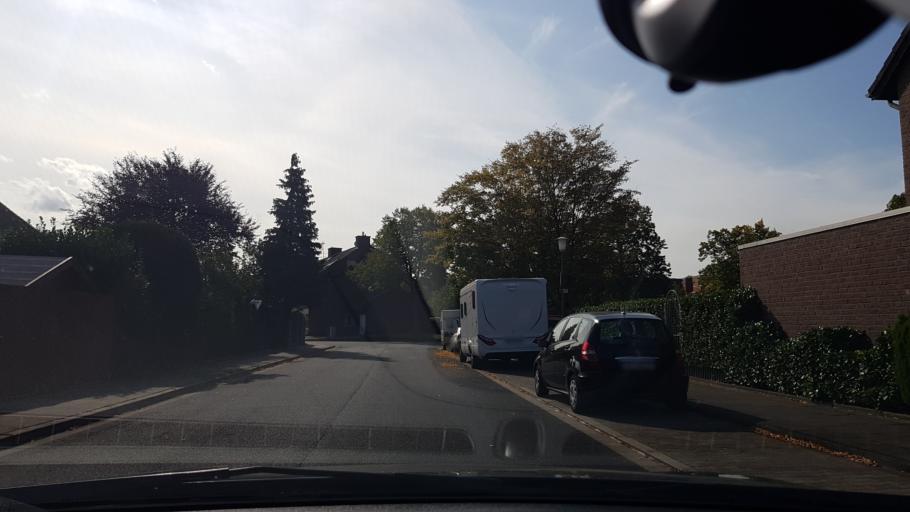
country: DE
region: North Rhine-Westphalia
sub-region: Regierungsbezirk Dusseldorf
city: Neuss
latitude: 51.1561
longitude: 6.7052
